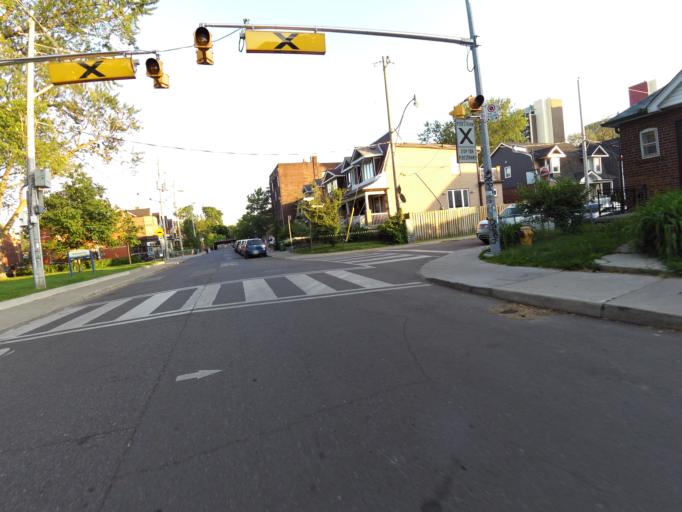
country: CA
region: Ontario
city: Toronto
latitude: 43.6468
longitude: -79.4344
